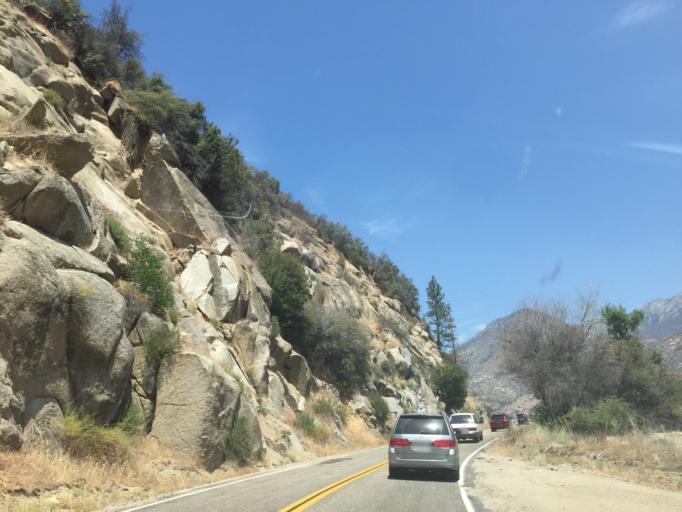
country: US
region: California
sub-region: Fresno County
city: Squaw Valley
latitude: 36.8308
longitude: -118.8738
